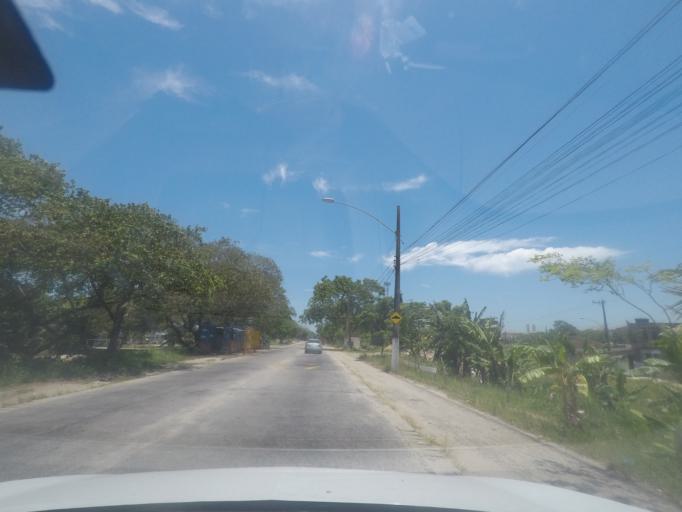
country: BR
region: Rio de Janeiro
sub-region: Itaguai
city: Itaguai
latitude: -22.9058
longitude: -43.6928
